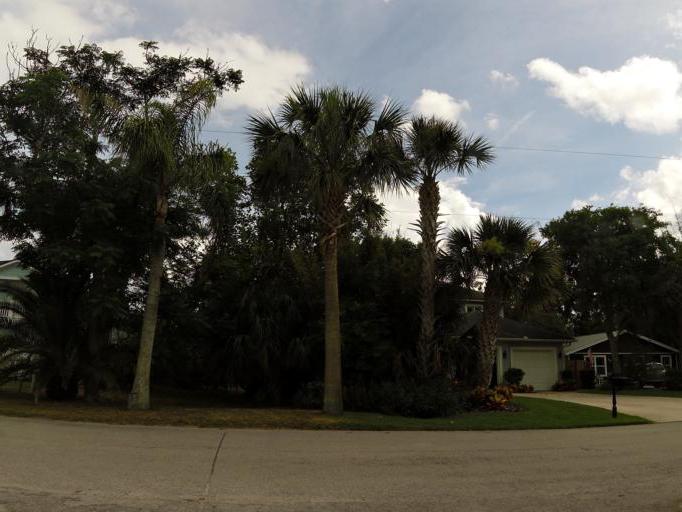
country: US
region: Florida
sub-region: Duval County
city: Jacksonville Beach
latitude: 30.2777
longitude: -81.3920
